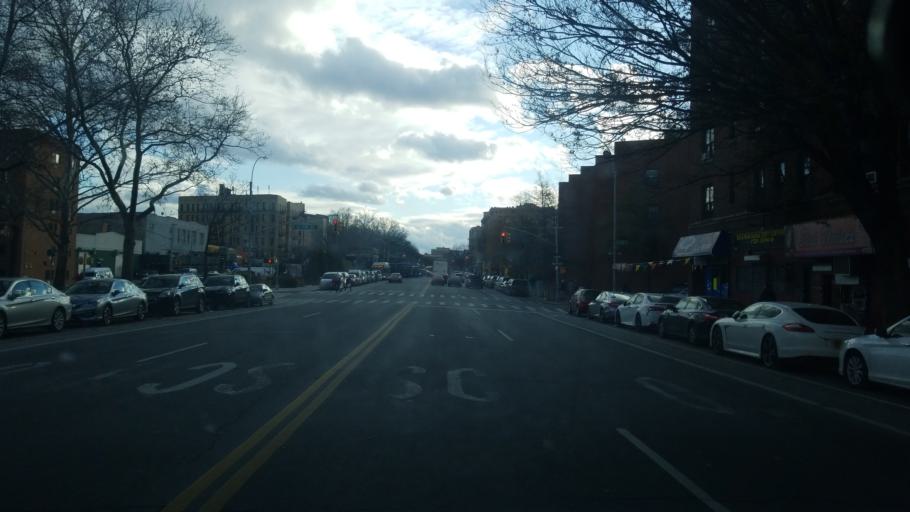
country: US
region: New York
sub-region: Bronx
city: The Bronx
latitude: 40.8443
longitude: -73.8854
